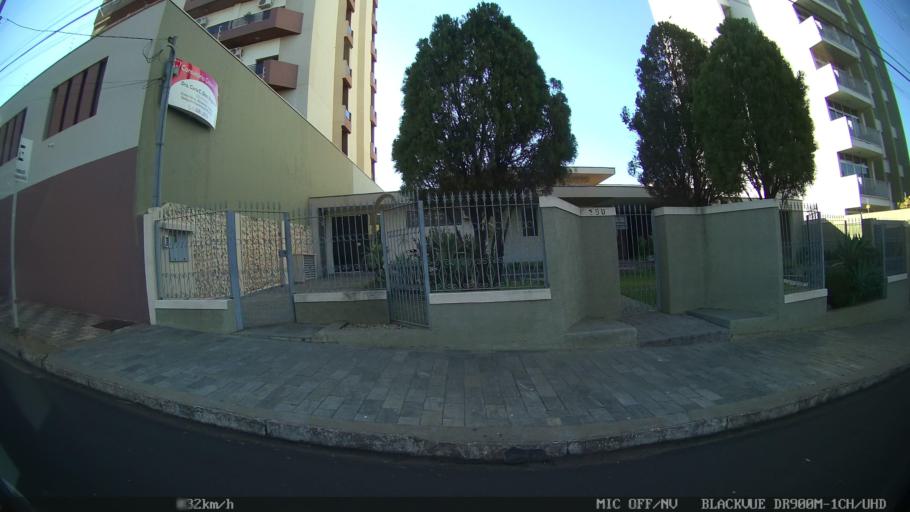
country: BR
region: Sao Paulo
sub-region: Olimpia
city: Olimpia
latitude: -20.7377
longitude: -48.9150
